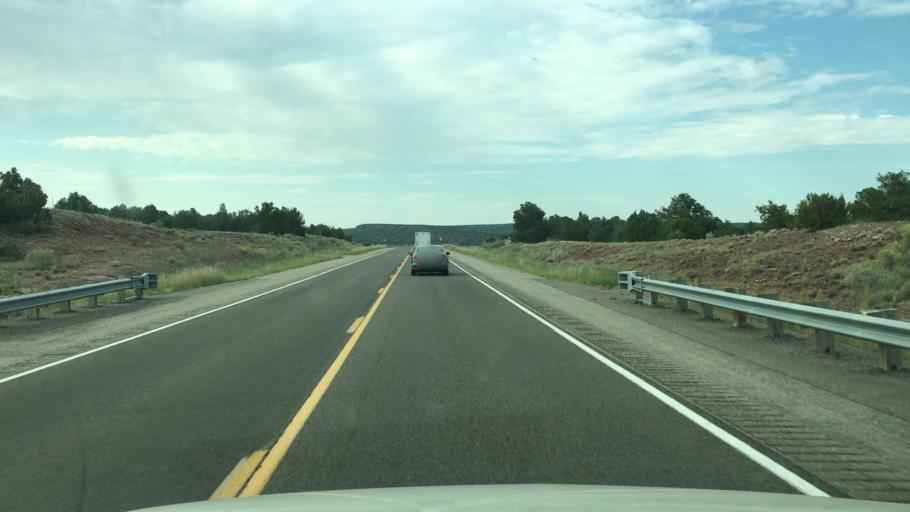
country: US
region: New Mexico
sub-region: Santa Fe County
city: Eldorado at Santa Fe
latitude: 35.2602
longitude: -105.8088
